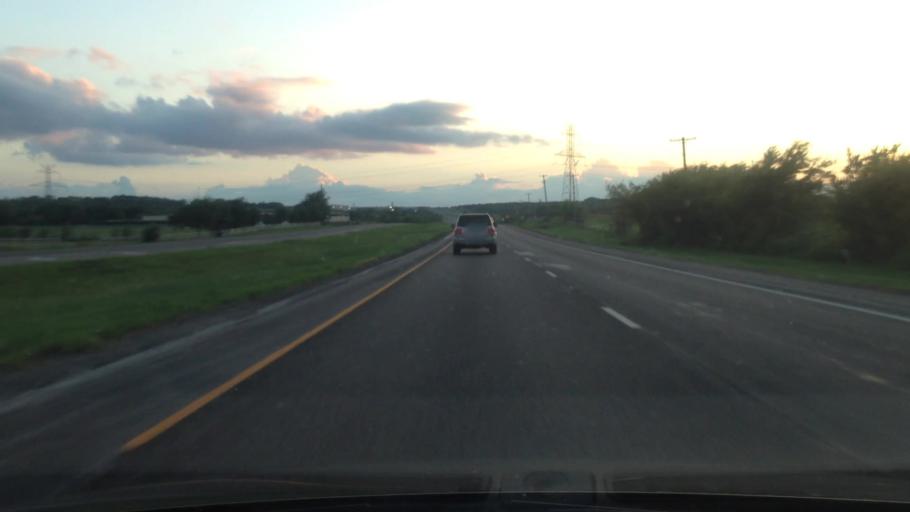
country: US
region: Texas
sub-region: Parker County
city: Aledo
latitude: 32.6014
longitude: -97.5662
